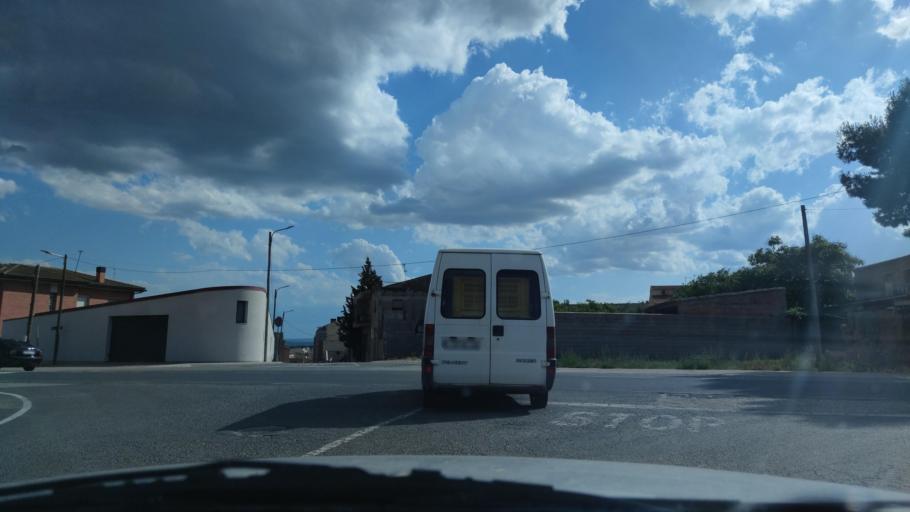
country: ES
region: Catalonia
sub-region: Provincia de Lleida
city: Alcarras
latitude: 41.5685
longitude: 0.5279
